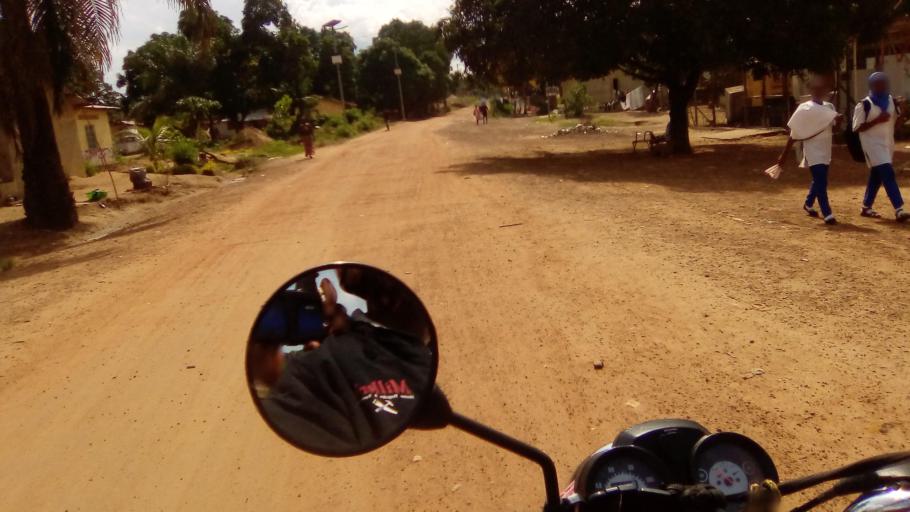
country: SL
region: Southern Province
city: Bo
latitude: 7.9492
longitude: -11.7216
